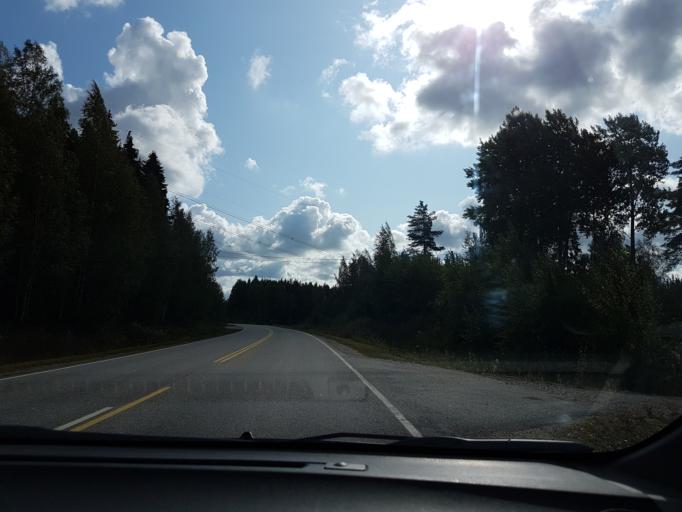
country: FI
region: Uusimaa
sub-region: Helsinki
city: Nickby
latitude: 60.4673
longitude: 25.2802
